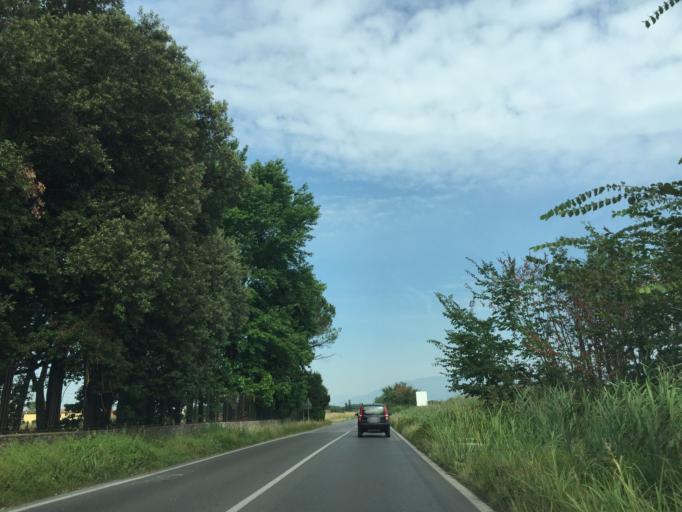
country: IT
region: Tuscany
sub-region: Provincia di Pistoia
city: Montecatini-Terme
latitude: 43.8542
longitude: 10.7811
